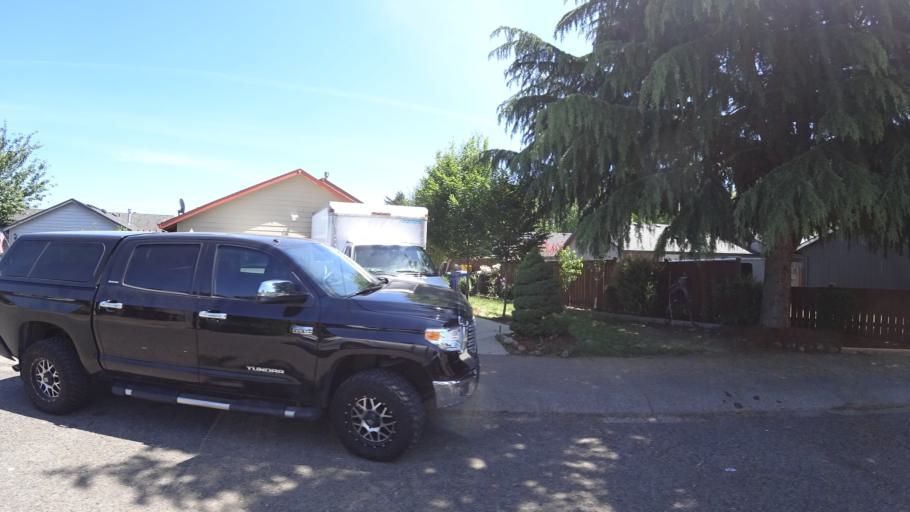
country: US
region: Oregon
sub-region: Multnomah County
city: Gresham
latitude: 45.4915
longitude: -122.4897
